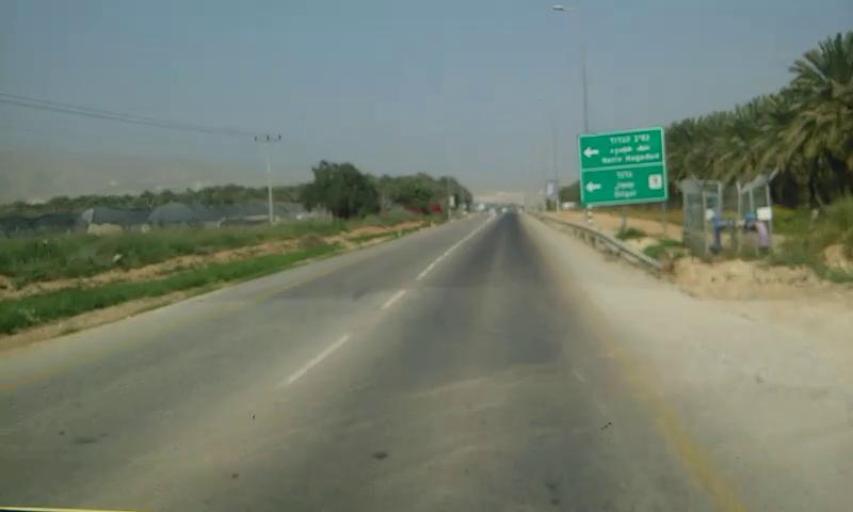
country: PS
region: West Bank
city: Al Fasayil
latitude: 31.9978
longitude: 35.4552
